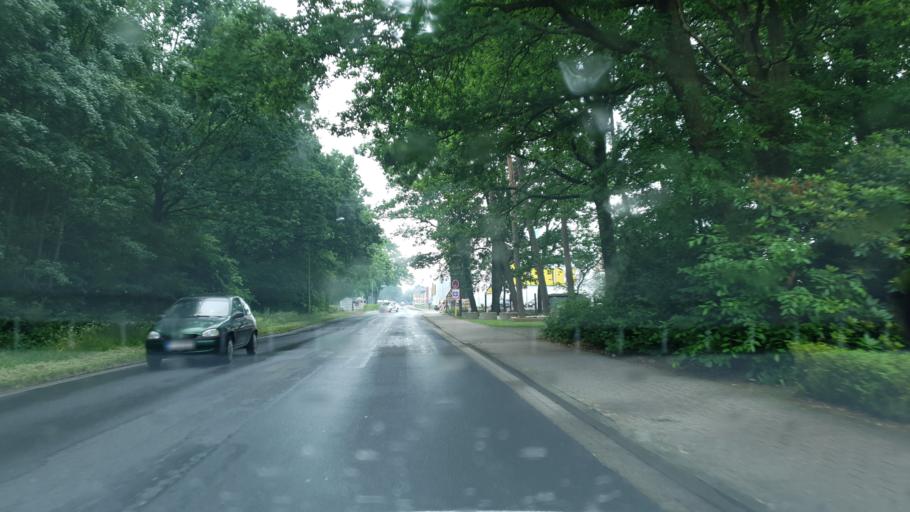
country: DE
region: Lower Saxony
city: Meppen
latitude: 52.6727
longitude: 7.3017
